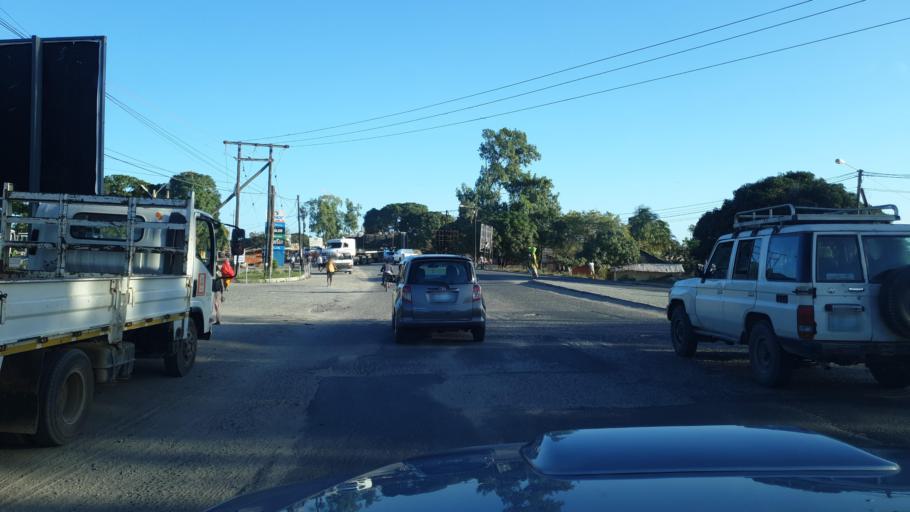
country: MZ
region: Nampula
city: Nacala
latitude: -14.5750
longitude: 40.6818
